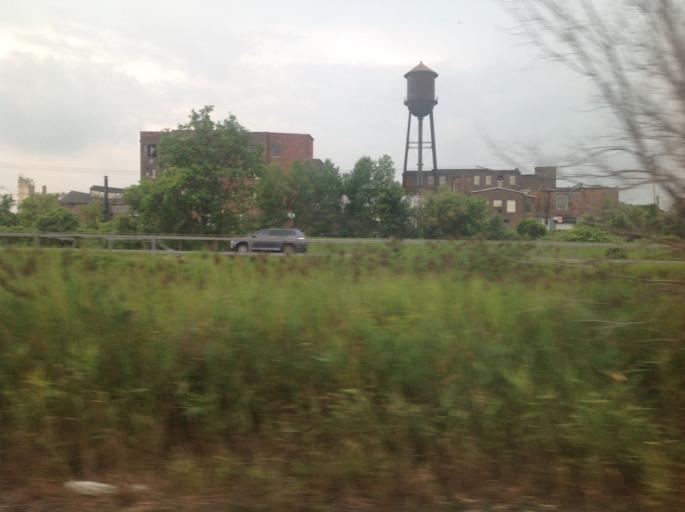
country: US
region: New York
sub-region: Oneida County
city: Utica
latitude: 43.1010
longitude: -75.2116
